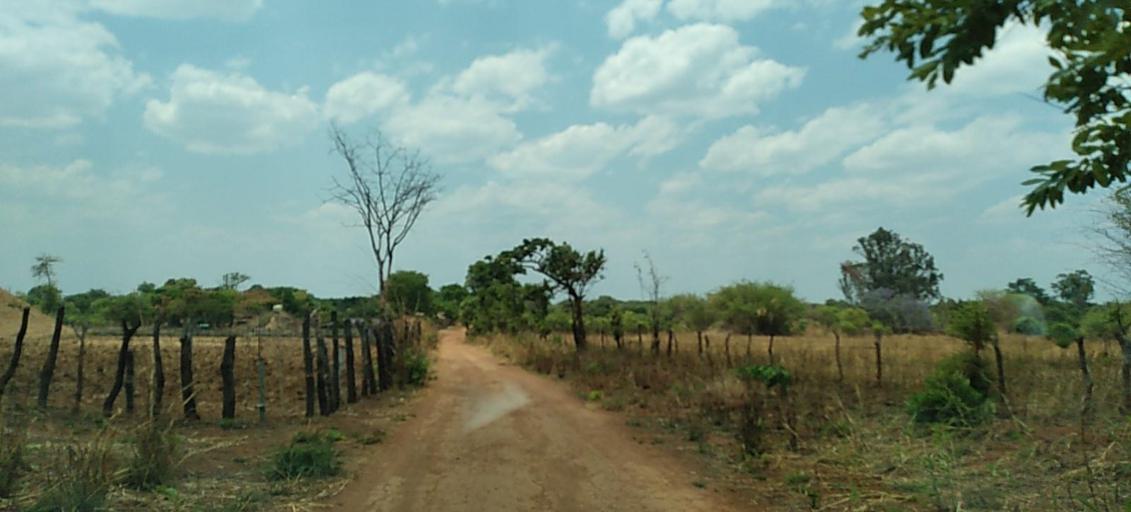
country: ZM
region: Copperbelt
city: Chingola
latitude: -12.5418
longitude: 27.6322
